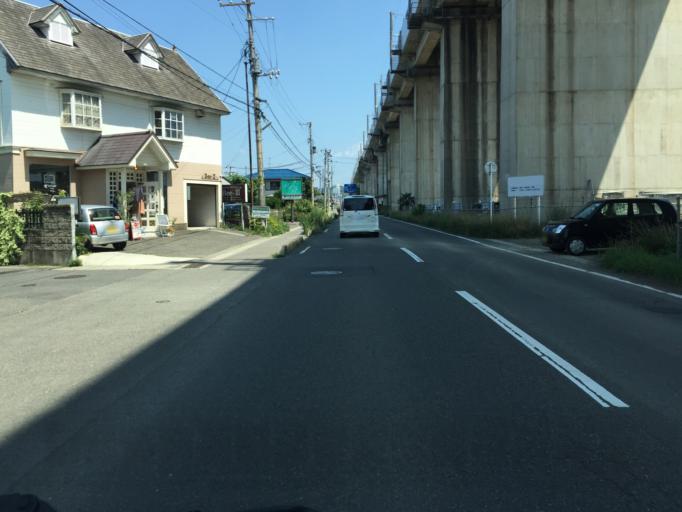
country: JP
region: Fukushima
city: Fukushima-shi
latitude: 37.7416
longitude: 140.4585
